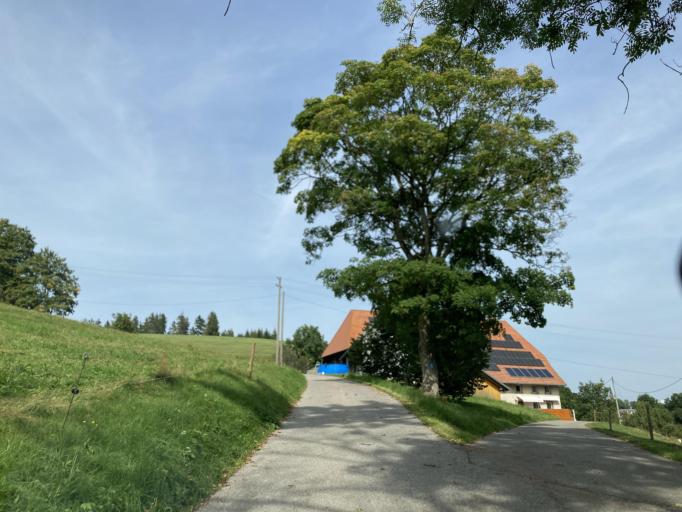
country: DE
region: Baden-Wuerttemberg
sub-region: Freiburg Region
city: Sankt Georgen im Schwarzwald
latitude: 48.1174
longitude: 8.3143
